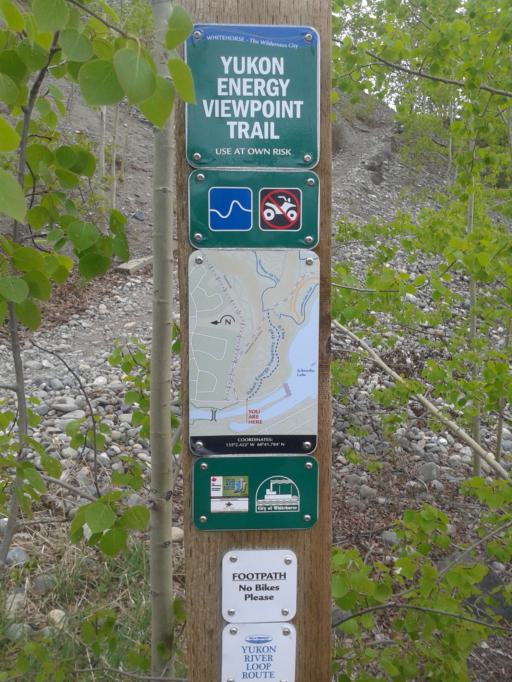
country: CA
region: Yukon
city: Whitehorse
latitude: 60.6964
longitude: -135.0403
